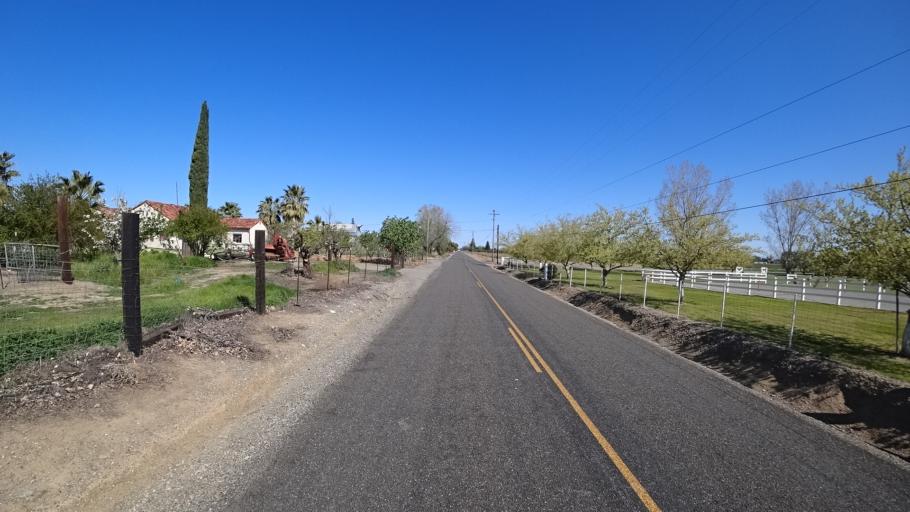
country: US
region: California
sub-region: Glenn County
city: Orland
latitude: 39.7325
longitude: -122.2158
